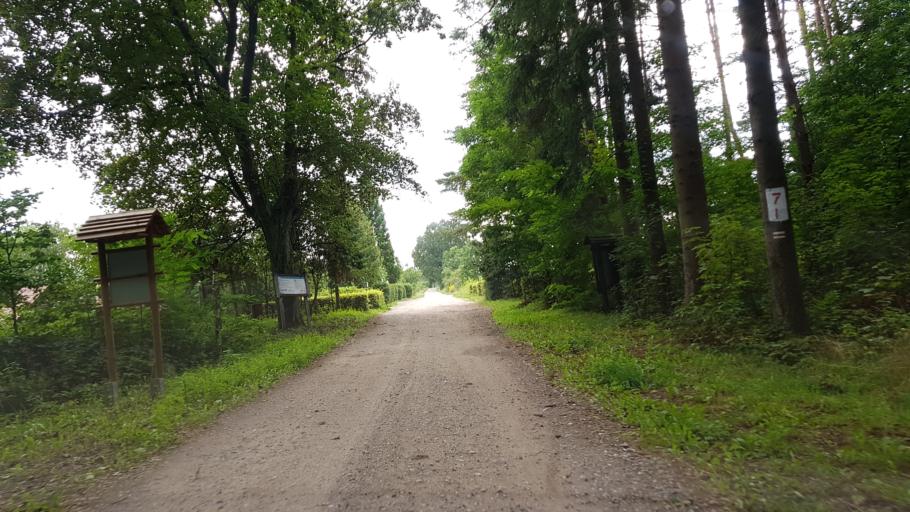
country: PL
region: West Pomeranian Voivodeship
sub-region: Powiat bialogardzki
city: Tychowo
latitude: 53.9994
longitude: 16.3044
